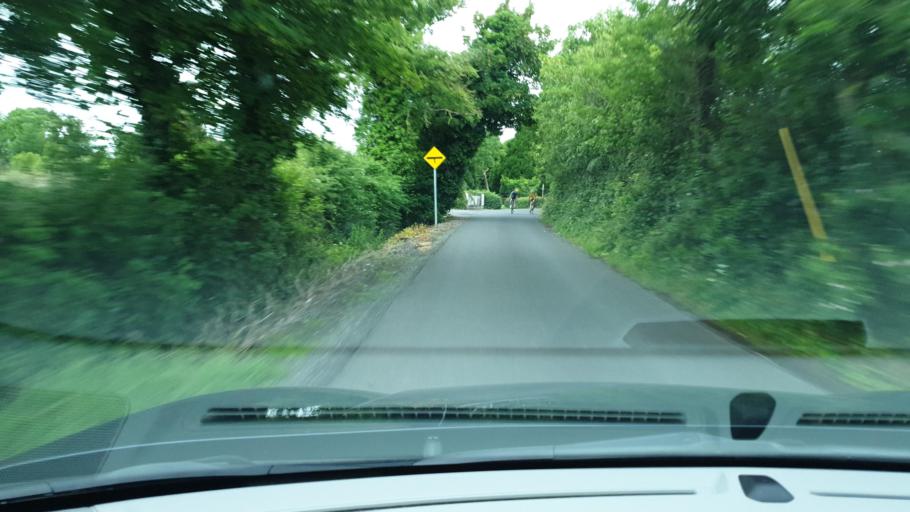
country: IE
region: Leinster
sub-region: An Mhi
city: Navan
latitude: 53.6414
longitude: -6.7224
